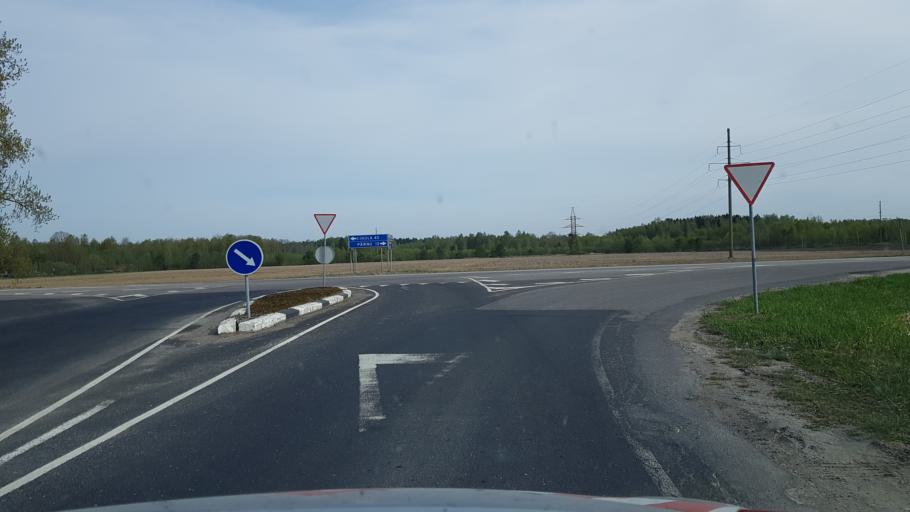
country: EE
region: Paernumaa
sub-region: Audru vald
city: Audru
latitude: 58.4225
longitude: 24.3084
